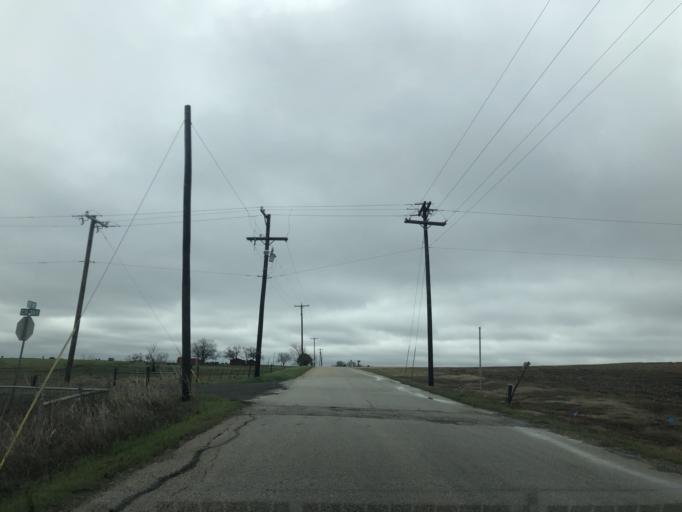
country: US
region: Texas
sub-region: Williamson County
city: Hutto
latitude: 30.5821
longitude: -97.4966
